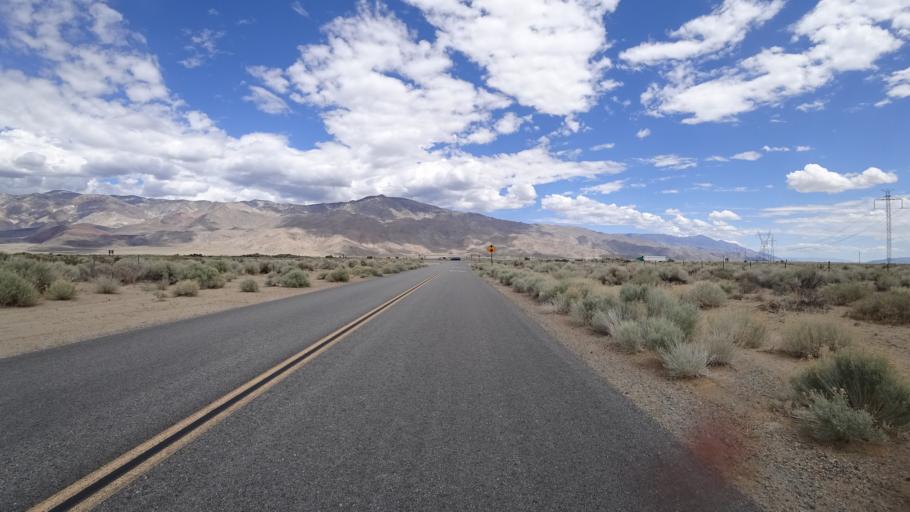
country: US
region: California
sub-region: Inyo County
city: Big Pine
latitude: 36.9786
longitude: -118.2375
